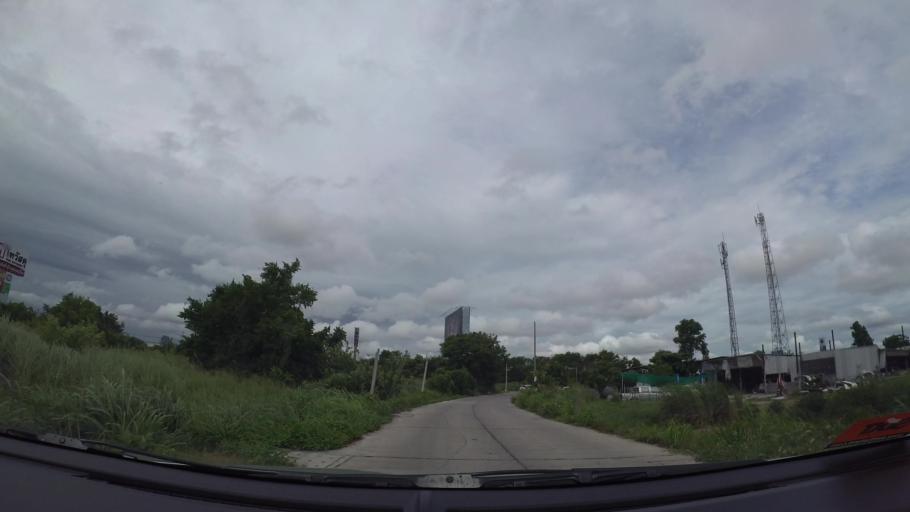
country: TH
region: Chon Buri
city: Si Racha
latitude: 13.1392
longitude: 100.9835
